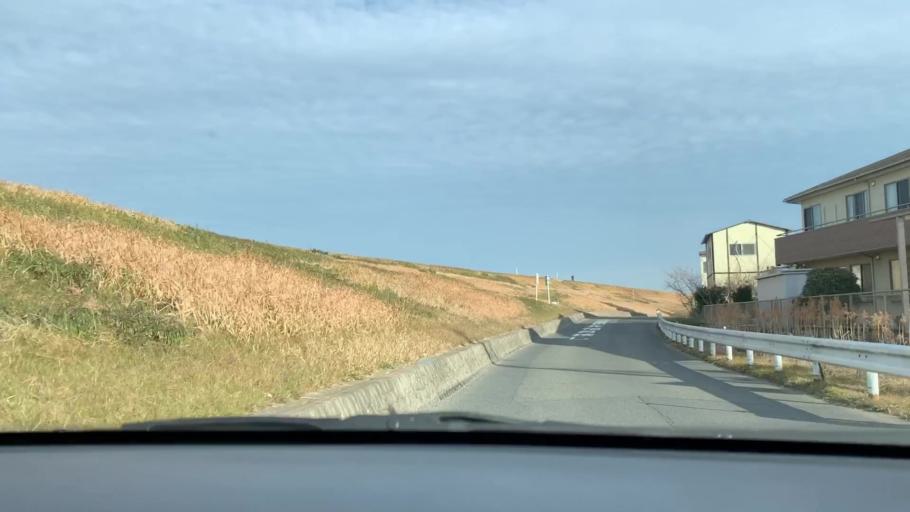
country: JP
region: Chiba
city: Matsudo
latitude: 35.8084
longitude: 139.8907
